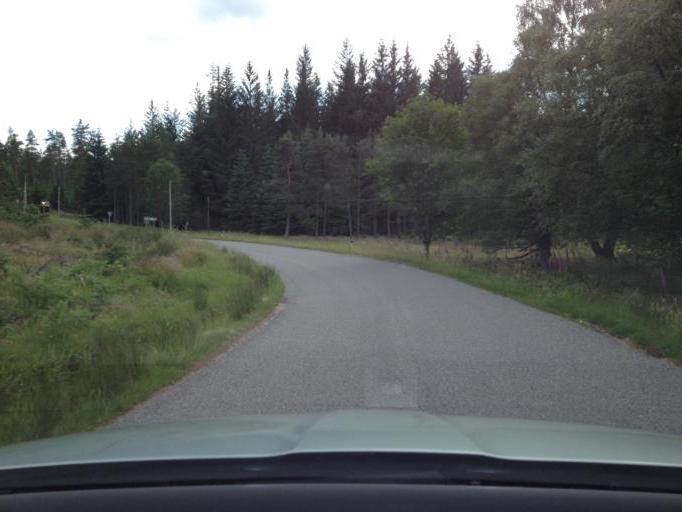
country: GB
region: Scotland
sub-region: Aberdeenshire
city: Banchory
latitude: 56.9924
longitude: -2.5763
